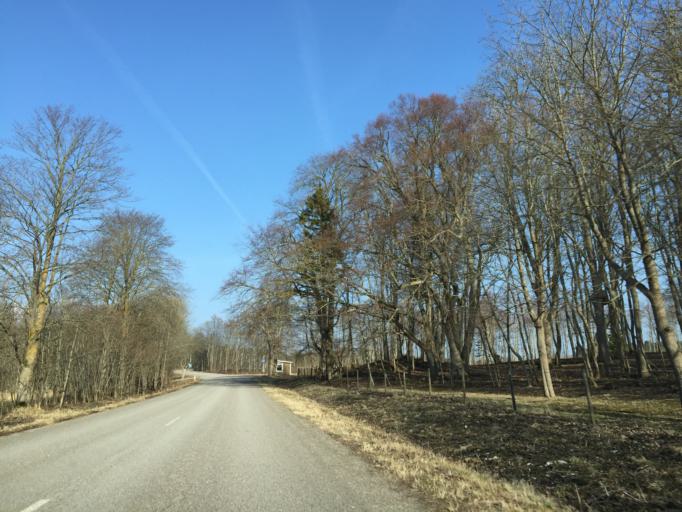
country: EE
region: Saare
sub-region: Kuressaare linn
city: Kuressaare
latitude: 58.0170
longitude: 22.0764
